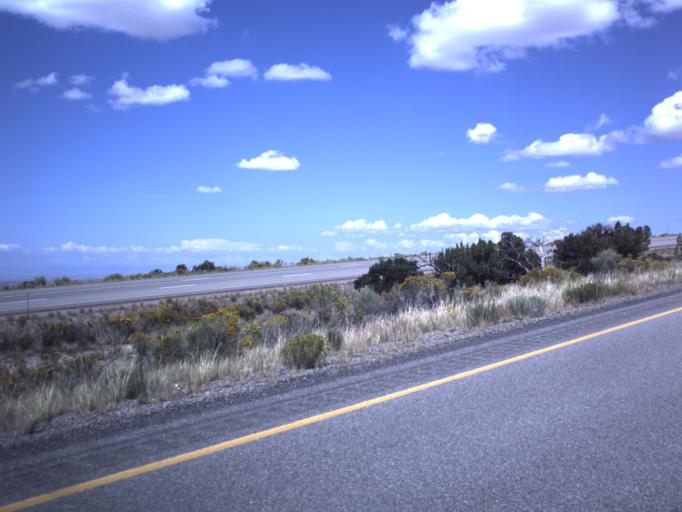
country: US
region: Utah
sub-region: Emery County
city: Ferron
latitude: 38.8460
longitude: -110.9431
